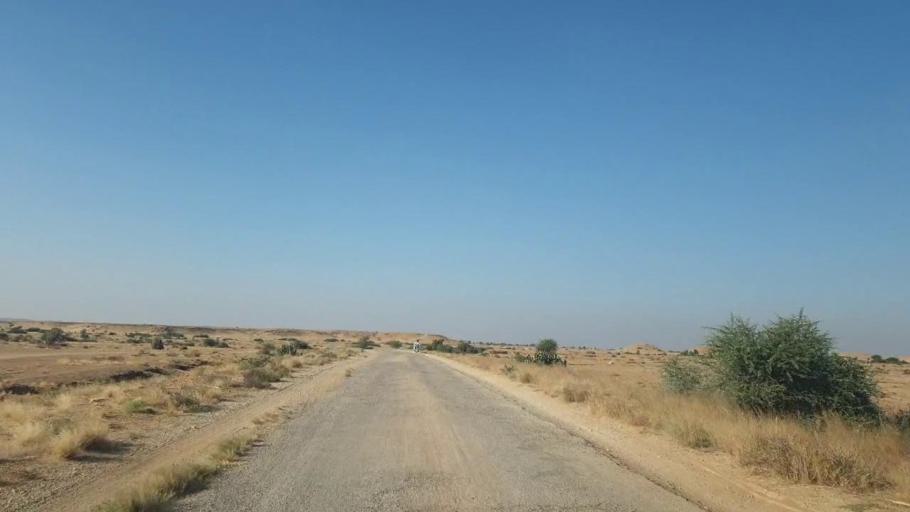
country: PK
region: Sindh
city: Malir Cantonment
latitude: 25.4086
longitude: 67.4668
